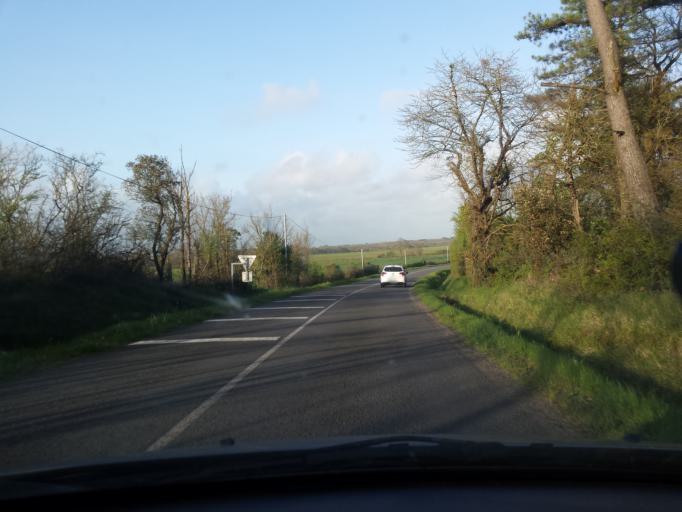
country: FR
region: Pays de la Loire
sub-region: Departement de la Vendee
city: Vaire
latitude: 46.5692
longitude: -1.7644
